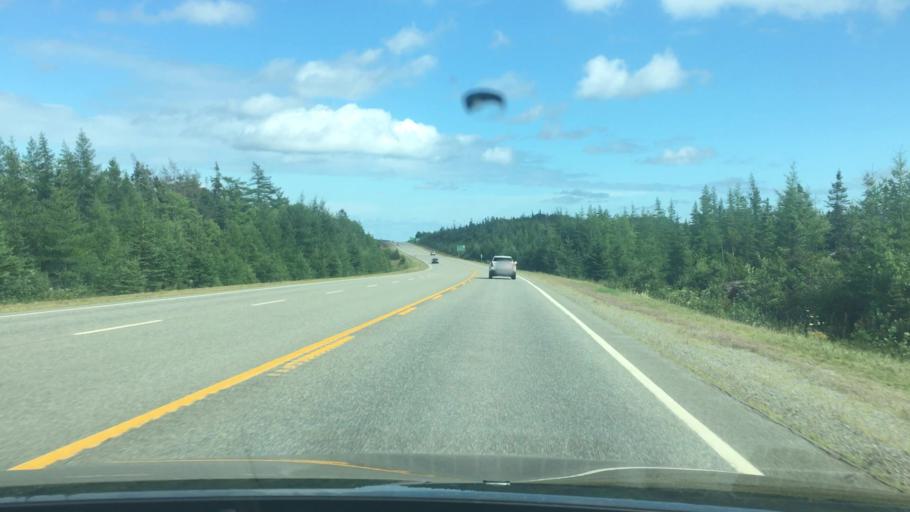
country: CA
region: Nova Scotia
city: Port Hawkesbury
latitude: 45.6162
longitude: -61.1006
